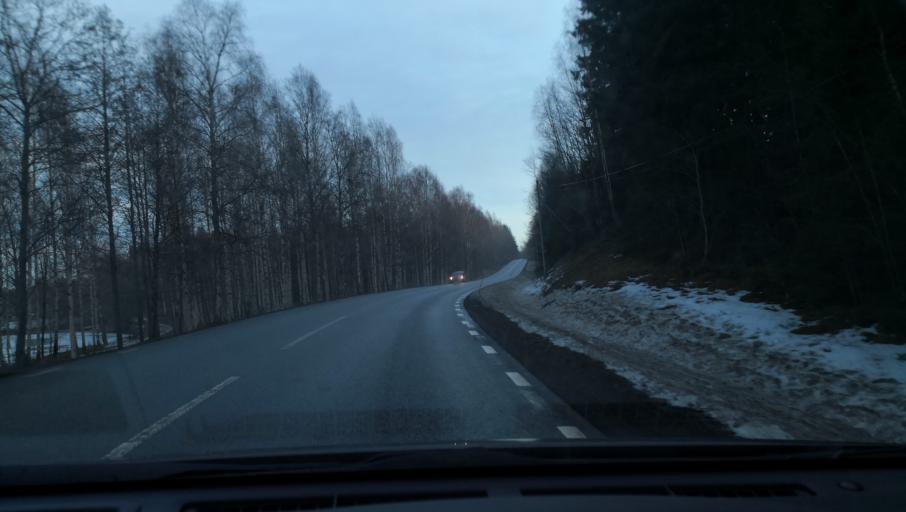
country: SE
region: OErebro
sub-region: Degerfors Kommun
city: Degerfors
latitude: 59.1300
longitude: 14.4981
